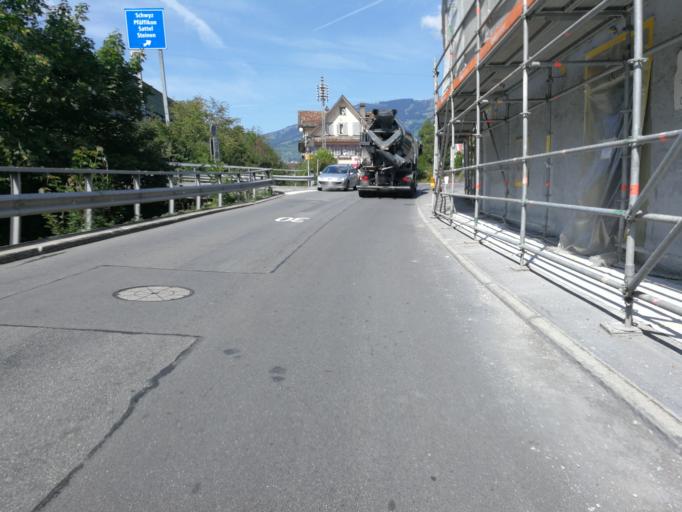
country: CH
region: Schwyz
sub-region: Bezirk Schwyz
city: Ibach
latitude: 47.0276
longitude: 8.6290
